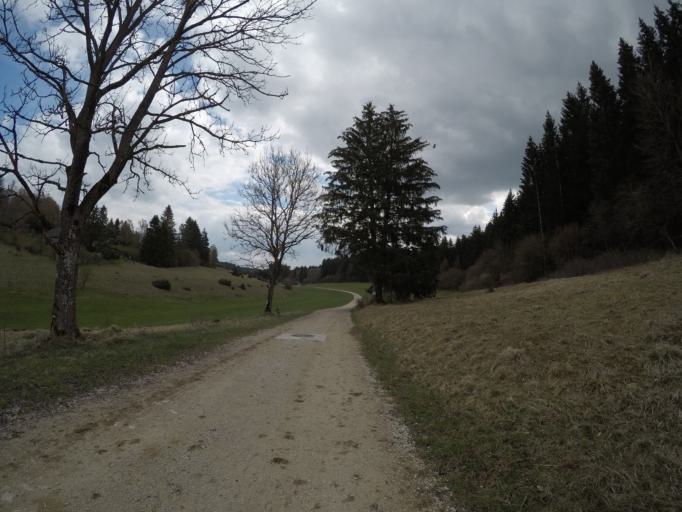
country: DE
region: Baden-Wuerttemberg
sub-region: Tuebingen Region
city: Merklingen
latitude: 48.5083
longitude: 9.7759
